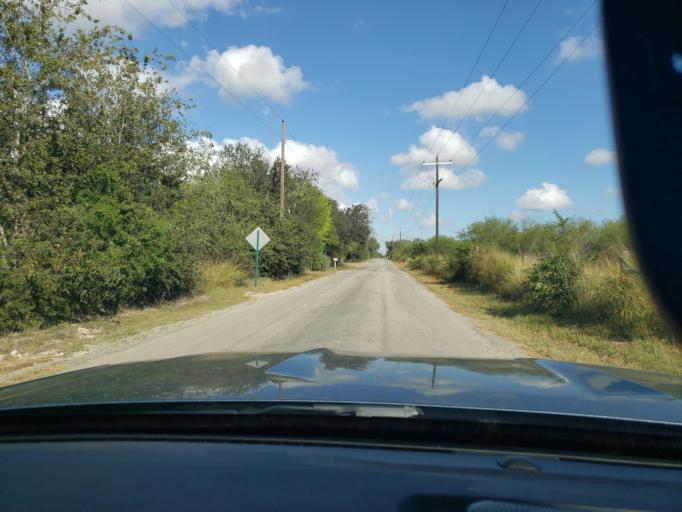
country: US
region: Texas
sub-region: Bee County
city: Beeville
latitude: 28.4421
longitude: -97.7138
